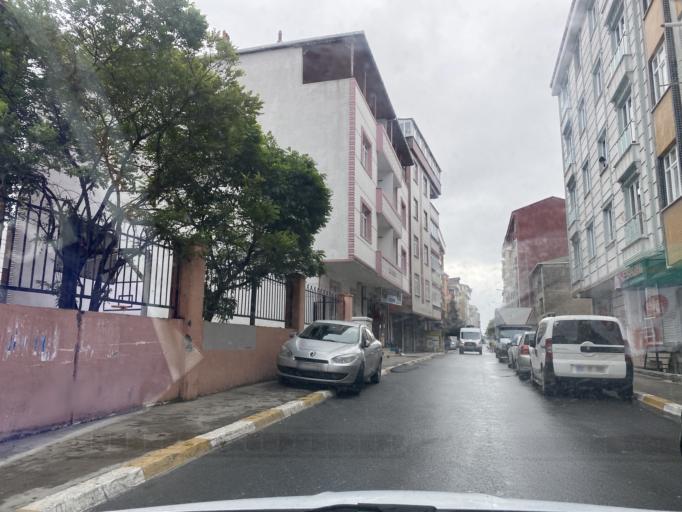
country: TR
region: Istanbul
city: Esenyurt
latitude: 41.0204
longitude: 28.6888
